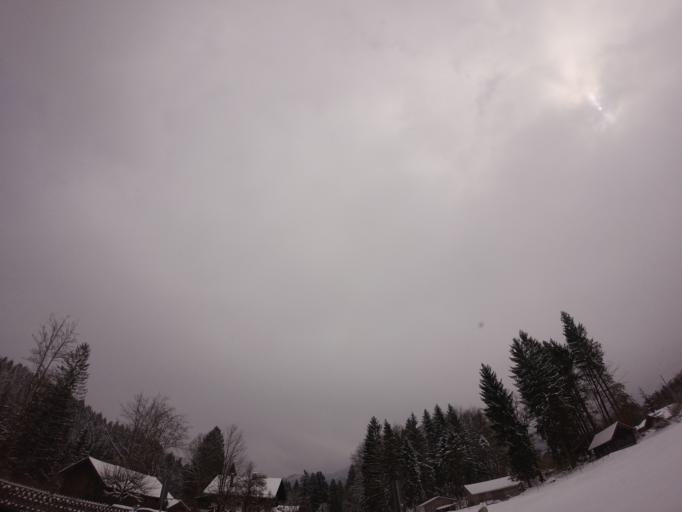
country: DE
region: Bavaria
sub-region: Upper Bavaria
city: Grainau
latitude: 47.4823
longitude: 11.0422
